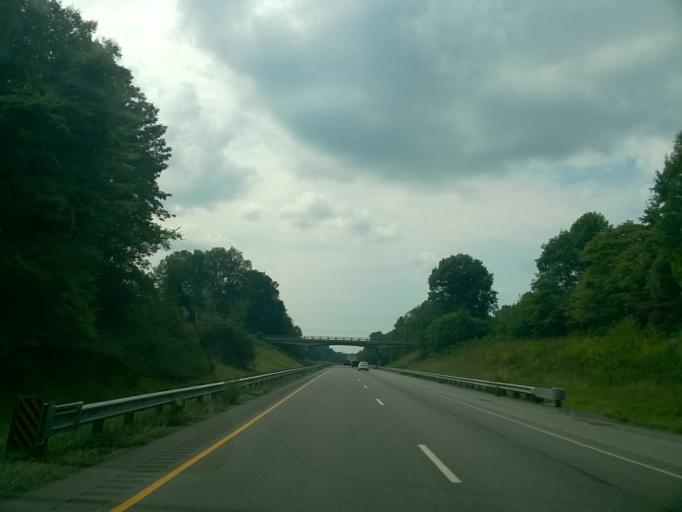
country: US
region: Indiana
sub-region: Putnam County
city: Cloverdale
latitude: 39.5182
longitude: -86.9075
